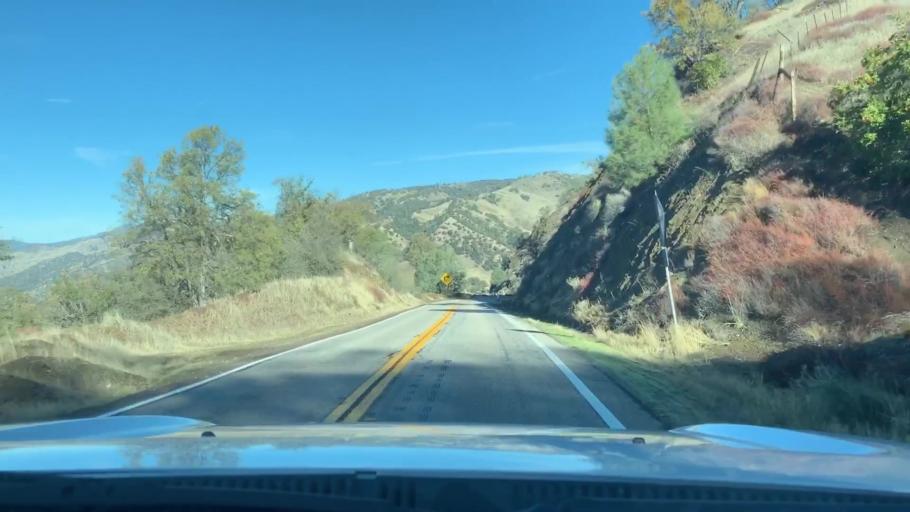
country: US
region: California
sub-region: Monterey County
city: King City
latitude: 36.1915
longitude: -120.7474
